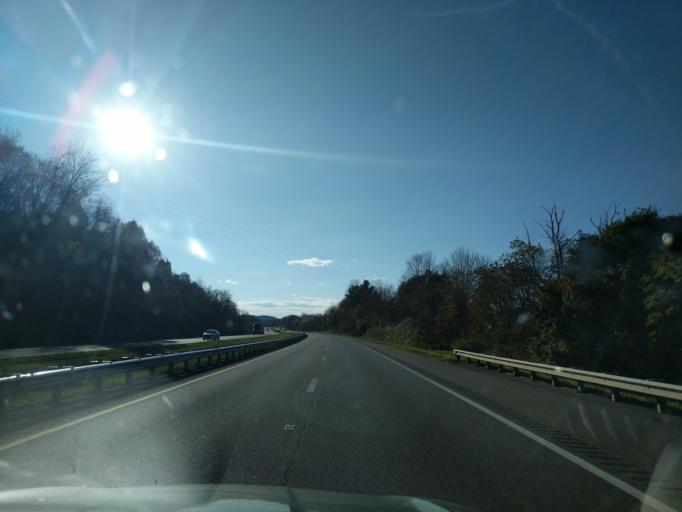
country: US
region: Virginia
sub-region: Smyth County
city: Marion
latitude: 36.8218
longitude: -81.5413
